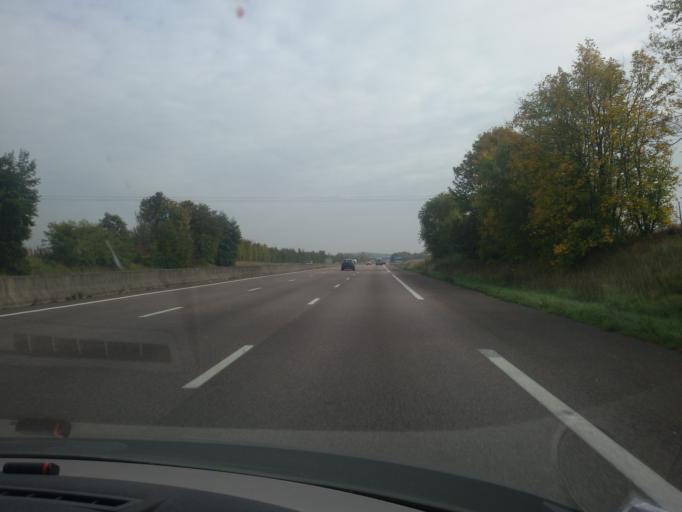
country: FR
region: Haute-Normandie
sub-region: Departement de l'Eure
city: La Chapelle-Reanville
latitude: 49.0718
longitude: 1.4052
